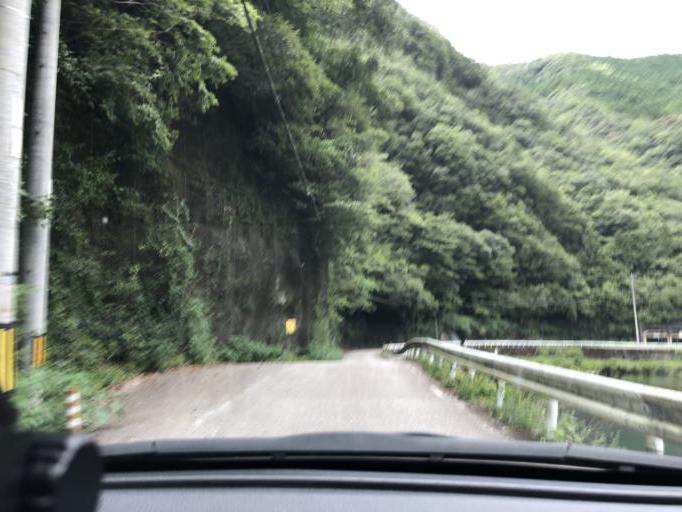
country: JP
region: Kochi
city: Kochi-shi
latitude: 33.6267
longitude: 133.5041
